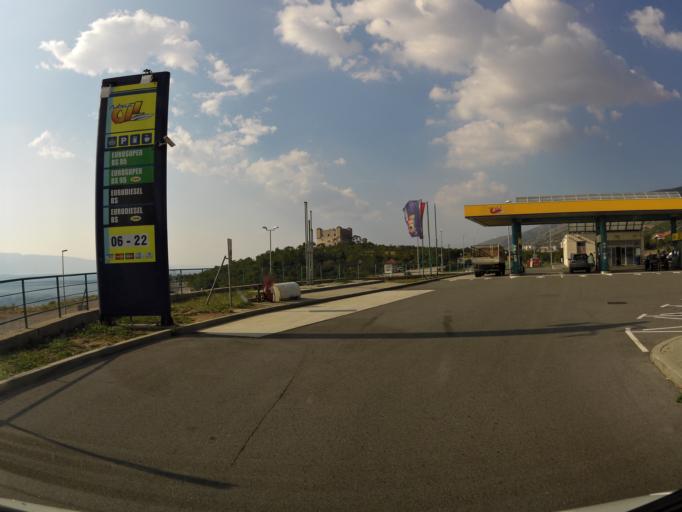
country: HR
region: Licko-Senjska
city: Senj
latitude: 44.9833
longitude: 14.9067
